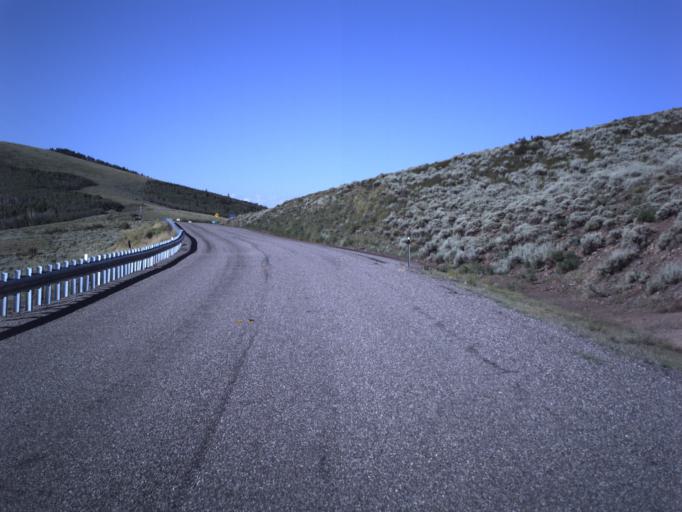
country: US
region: Utah
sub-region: Wayne County
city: Loa
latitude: 38.5859
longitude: -111.4760
